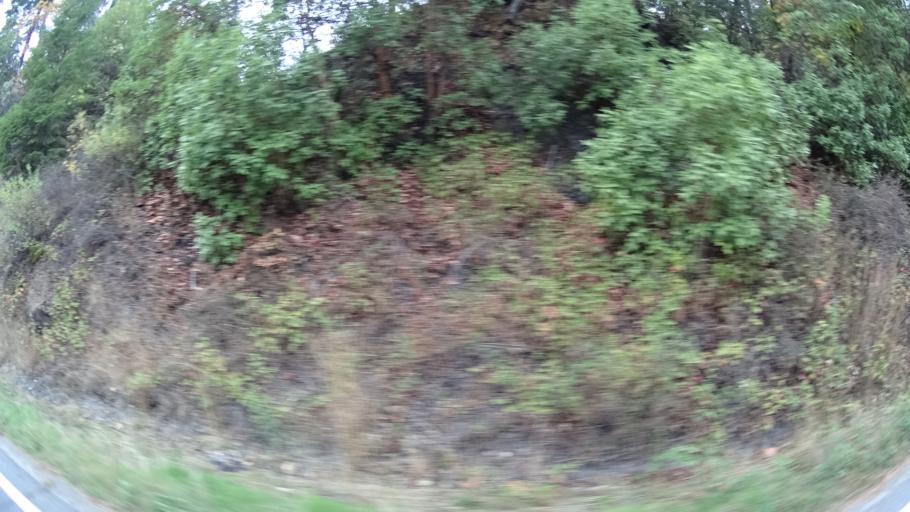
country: US
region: California
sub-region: Siskiyou County
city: Happy Camp
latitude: 41.7806
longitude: -123.3956
